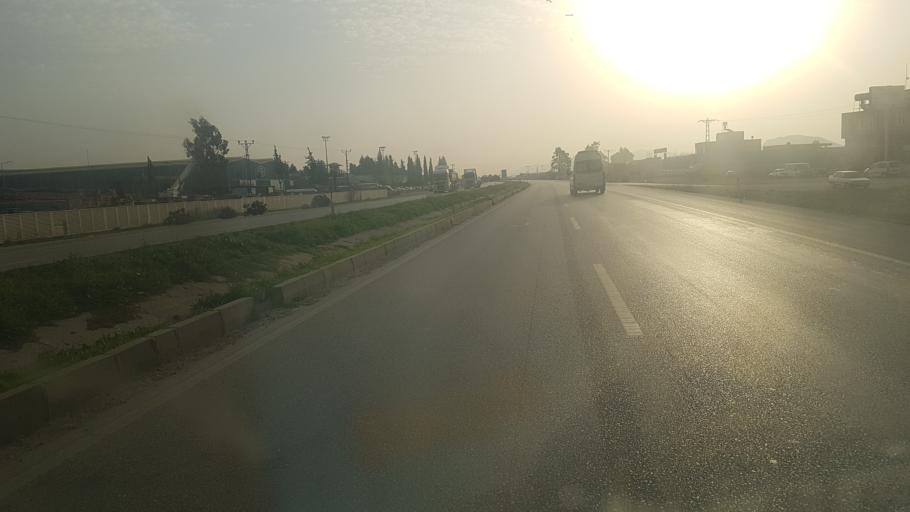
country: TR
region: Adana
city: Ceyhan
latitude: 37.0512
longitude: 35.8209
